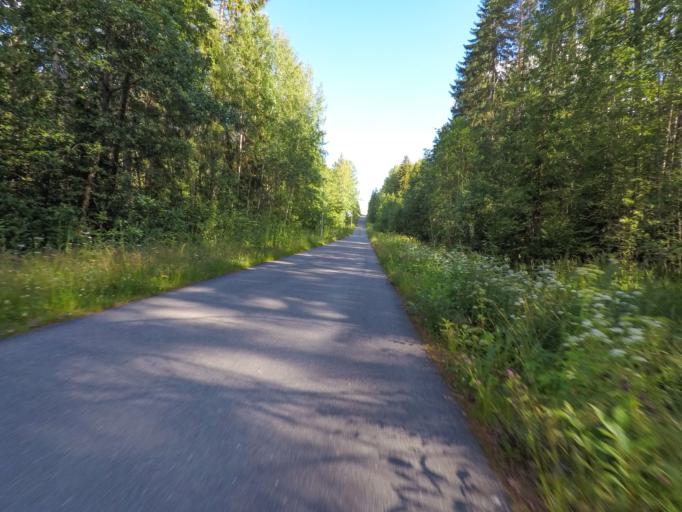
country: FI
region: South Karelia
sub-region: Lappeenranta
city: Lappeenranta
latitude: 61.0936
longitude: 28.1387
